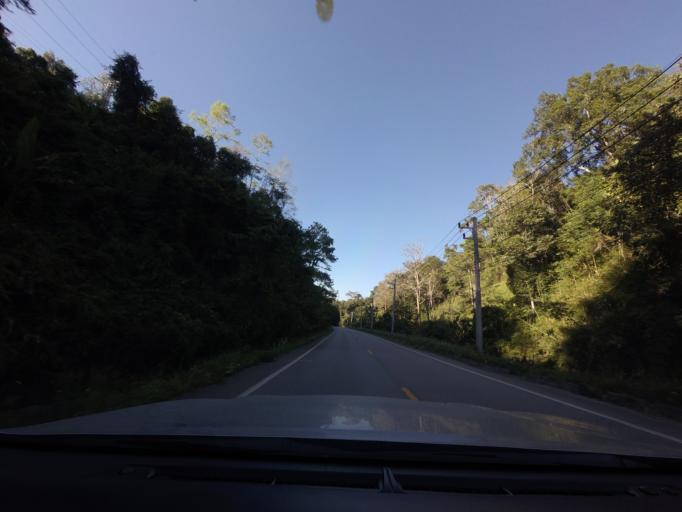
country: TH
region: Chiang Mai
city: Mae Taeng
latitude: 19.1897
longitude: 98.6912
